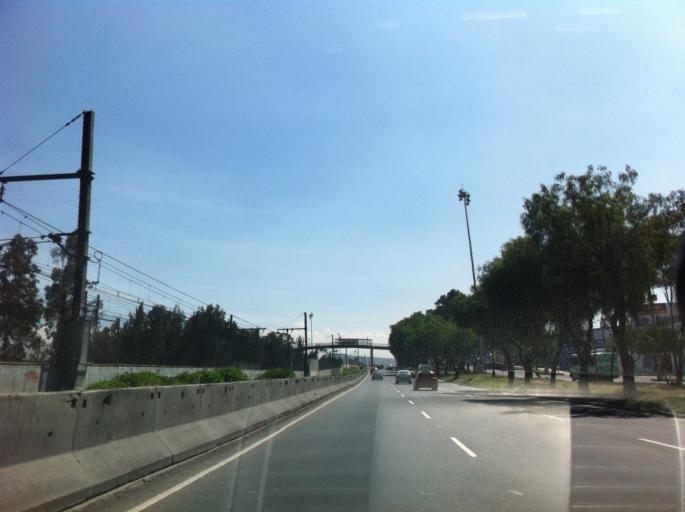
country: MX
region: Mexico
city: Ciudad Nezahualcoyotl
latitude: 19.3716
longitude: -99.0148
